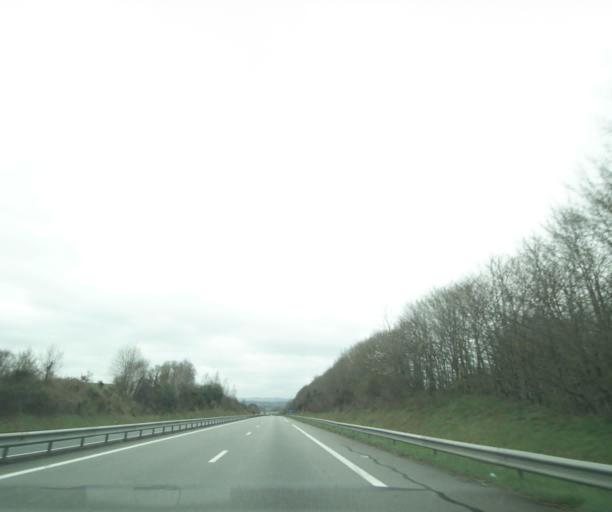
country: FR
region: Limousin
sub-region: Departement de la Creuse
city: Saint-Maurice-la-Souterraine
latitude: 46.1826
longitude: 1.3804
